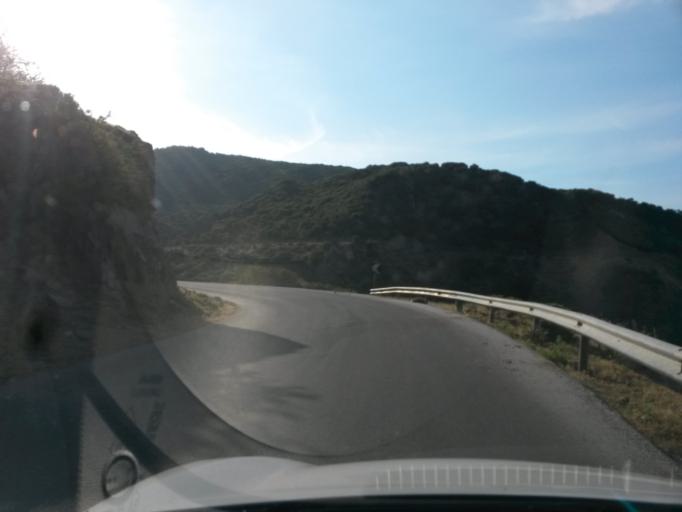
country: GR
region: North Aegean
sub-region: Nomos Lesvou
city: Mantamados
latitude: 39.3474
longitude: 26.3063
